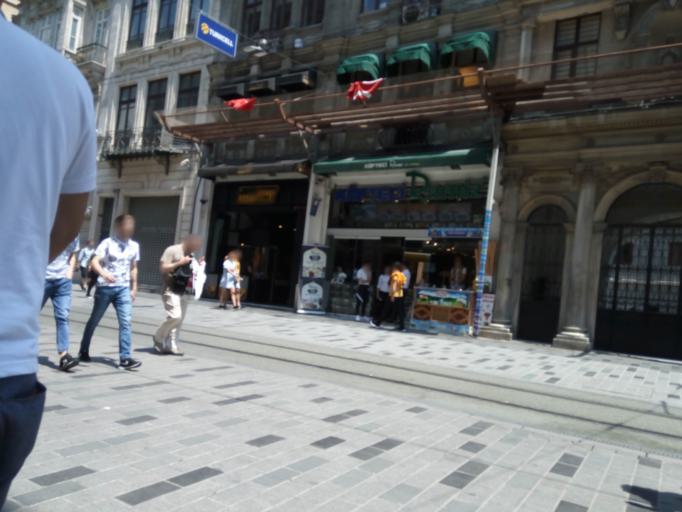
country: TR
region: Istanbul
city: Eminoenue
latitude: 41.0300
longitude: 28.9758
